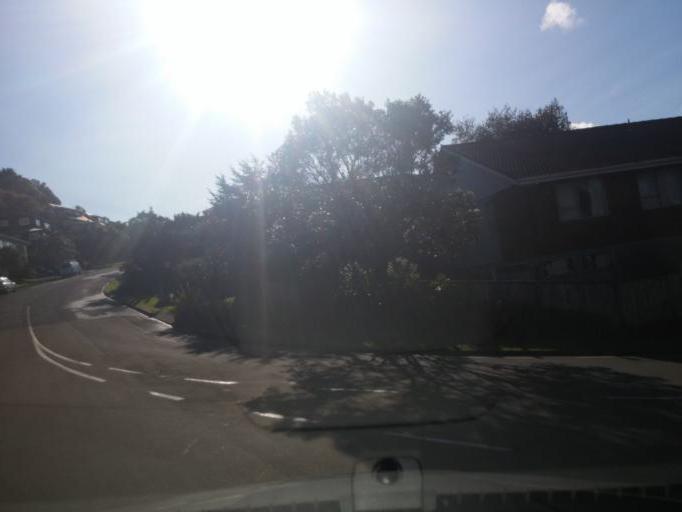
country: NZ
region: Wellington
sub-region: Wellington City
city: Wellington
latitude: -41.2359
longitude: 174.7976
